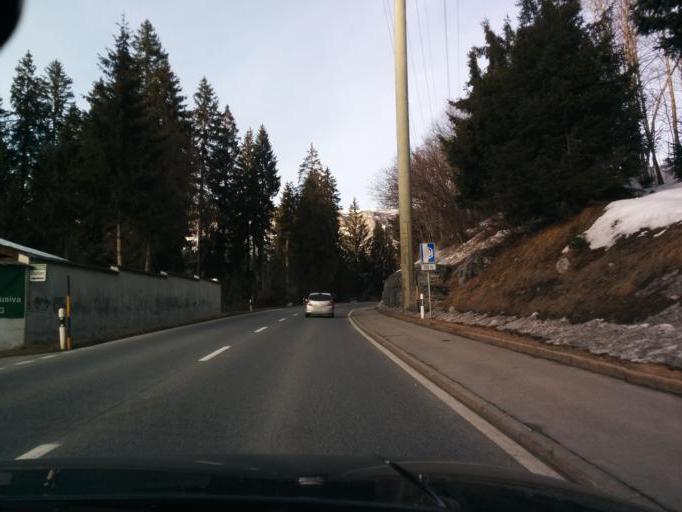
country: CH
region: Grisons
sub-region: Surselva District
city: Laax
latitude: 46.8197
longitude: 9.2681
